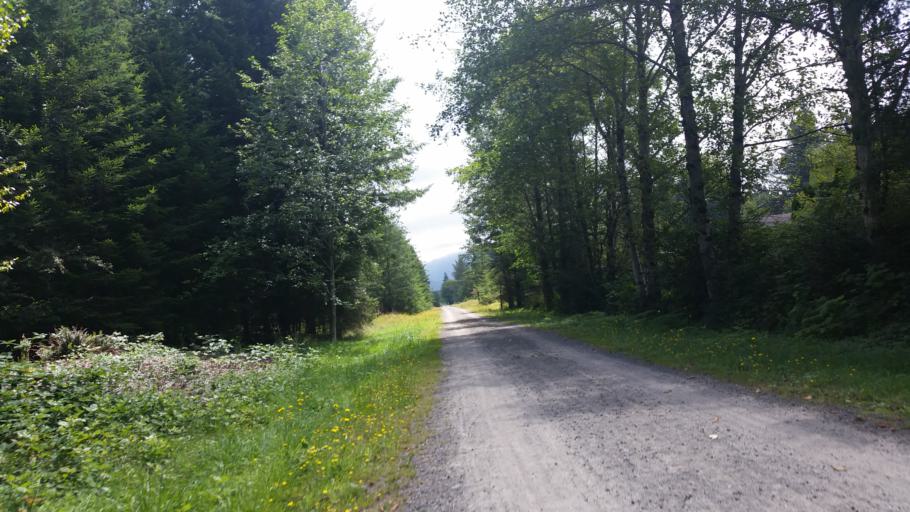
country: US
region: Washington
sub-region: King County
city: Tanner
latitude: 47.4874
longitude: -121.7650
